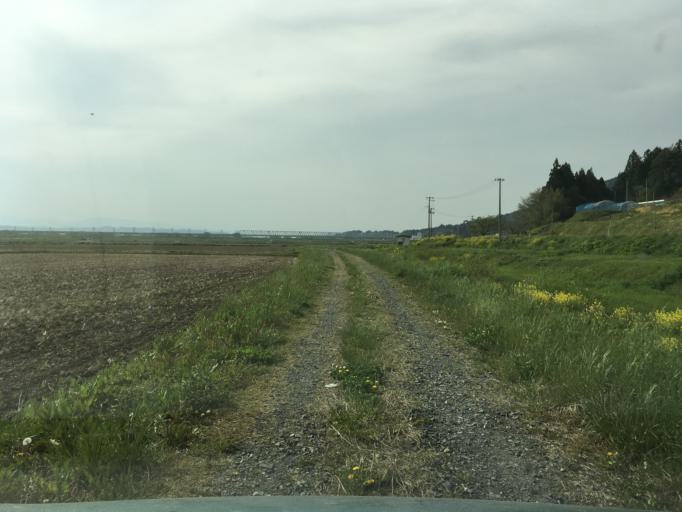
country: JP
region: Iwate
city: Ichinoseki
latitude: 38.9637
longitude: 141.1683
